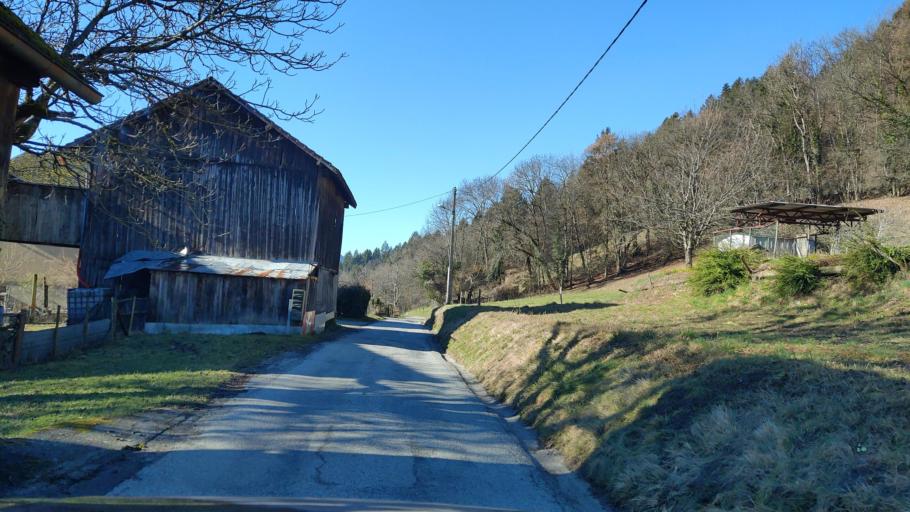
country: FR
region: Rhone-Alpes
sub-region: Departement de la Savoie
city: La Rochette
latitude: 45.4599
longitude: 6.0986
